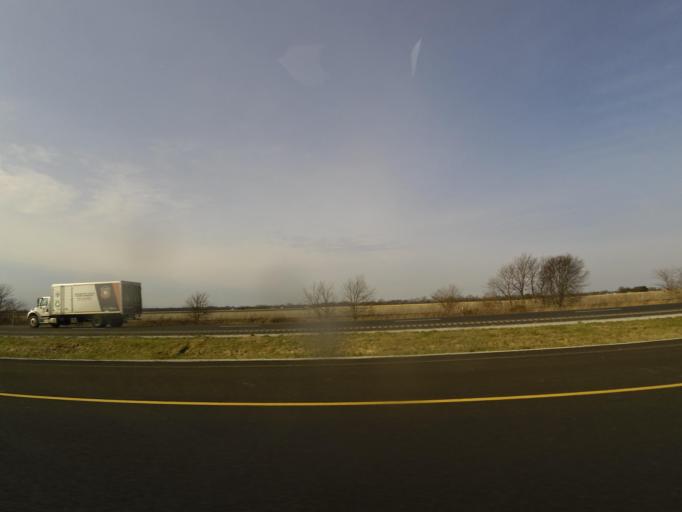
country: US
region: Illinois
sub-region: Shelby County
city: Moweaqua
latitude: 39.6689
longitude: -89.0087
